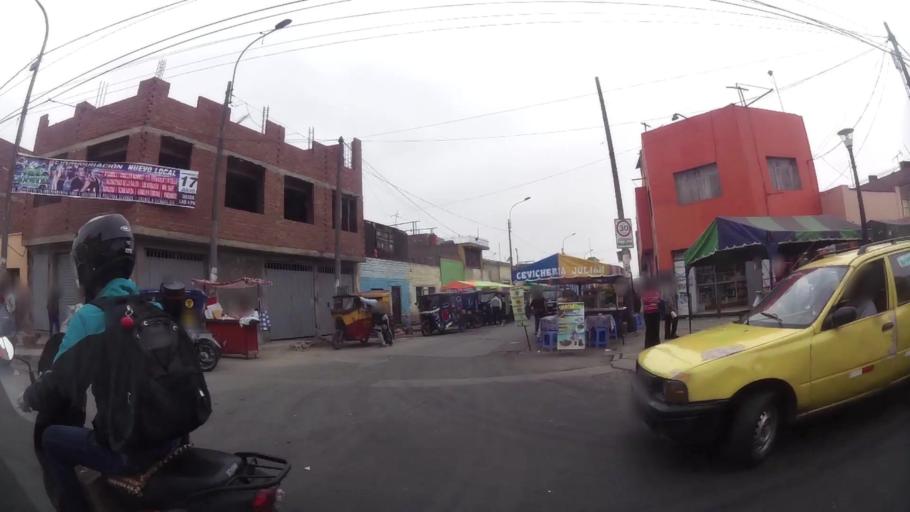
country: PE
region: Lima
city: Lima
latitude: -12.0463
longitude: -77.0156
